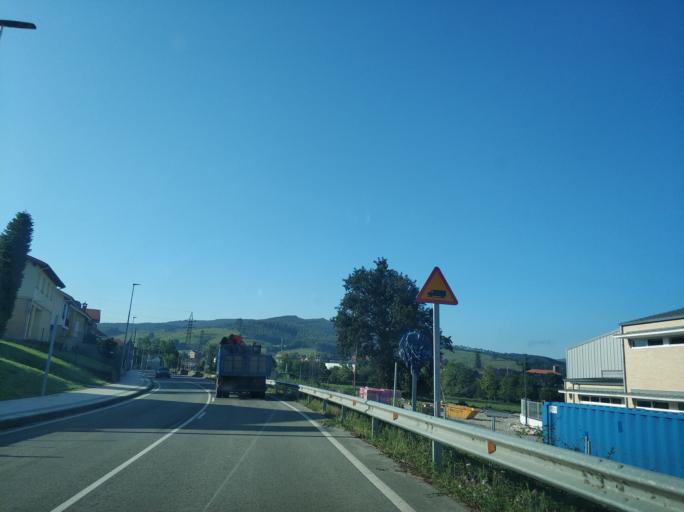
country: ES
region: Cantabria
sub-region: Provincia de Cantabria
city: Polanco
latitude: 43.3615
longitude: -3.9570
